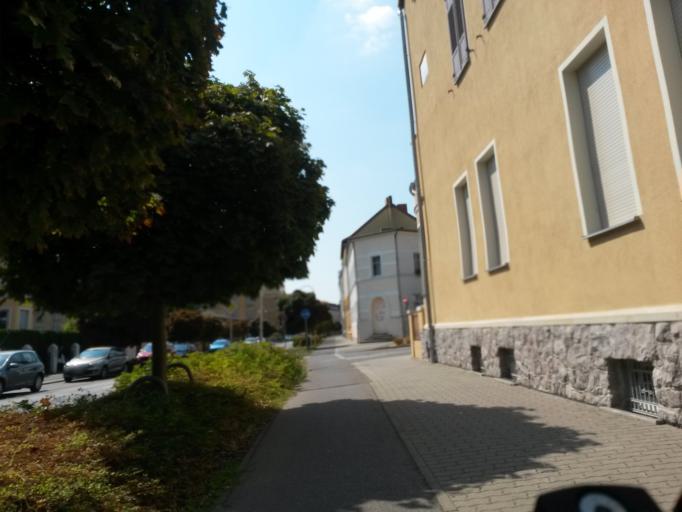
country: DE
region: Saxony-Anhalt
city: Wittenburg
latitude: 51.8696
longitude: 12.6574
